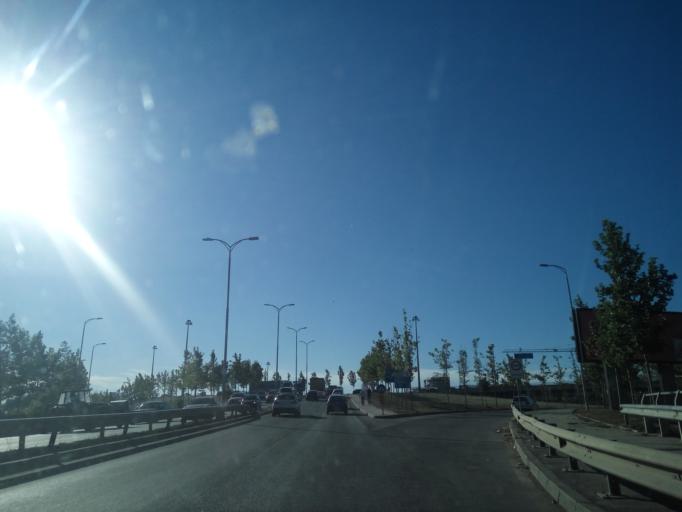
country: XK
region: Pristina
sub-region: Komuna e Prishtines
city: Pristina
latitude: 42.6514
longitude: 21.1479
